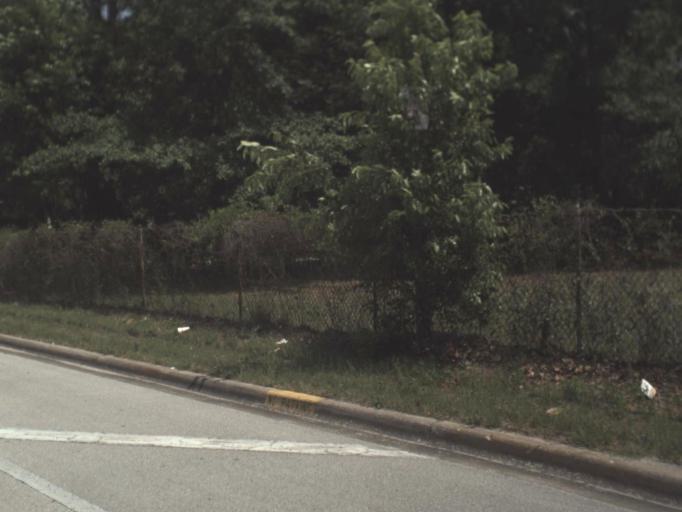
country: US
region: Florida
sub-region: Clay County
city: Bellair-Meadowbrook Terrace
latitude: 30.2898
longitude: -81.7900
